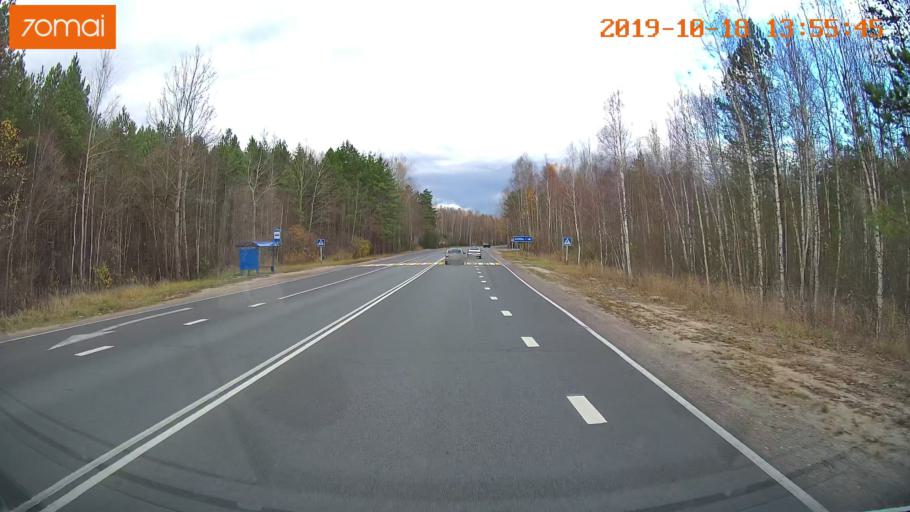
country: RU
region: Rjazan
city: Spas-Klepiki
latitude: 55.0557
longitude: 40.0248
